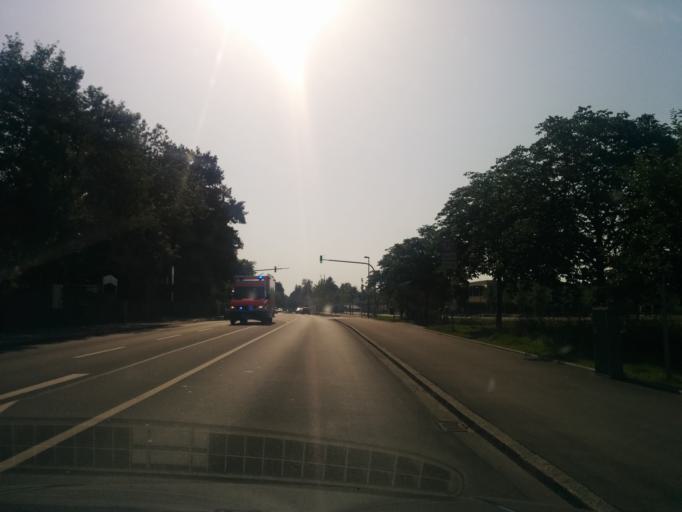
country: DE
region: Bavaria
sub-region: Upper Bavaria
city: Grunwald
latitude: 48.0387
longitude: 11.5243
